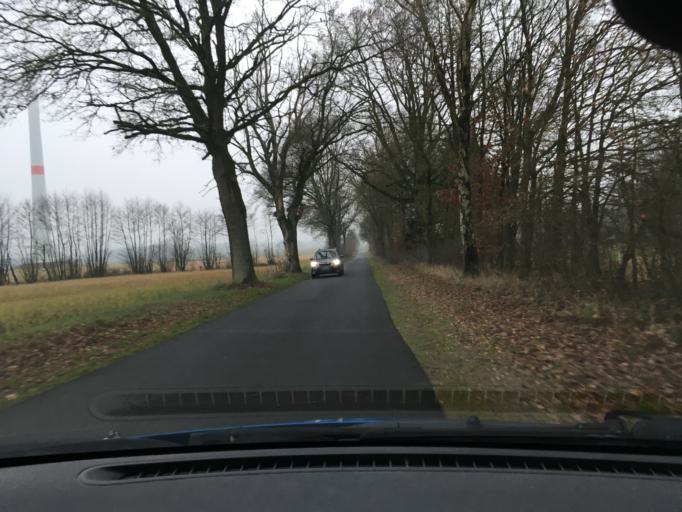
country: DE
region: Lower Saxony
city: Soderstorf
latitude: 53.0991
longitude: 10.1649
